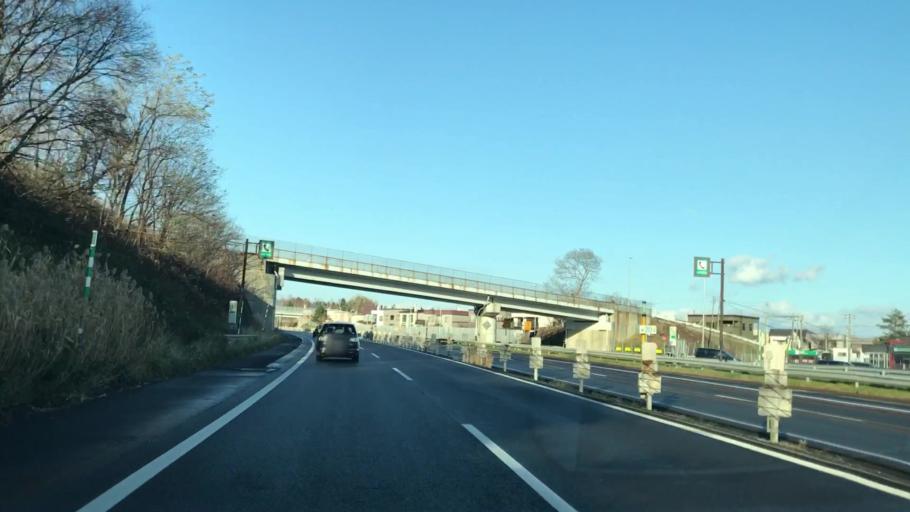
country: JP
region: Hokkaido
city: Sapporo
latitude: 43.1244
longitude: 141.2110
